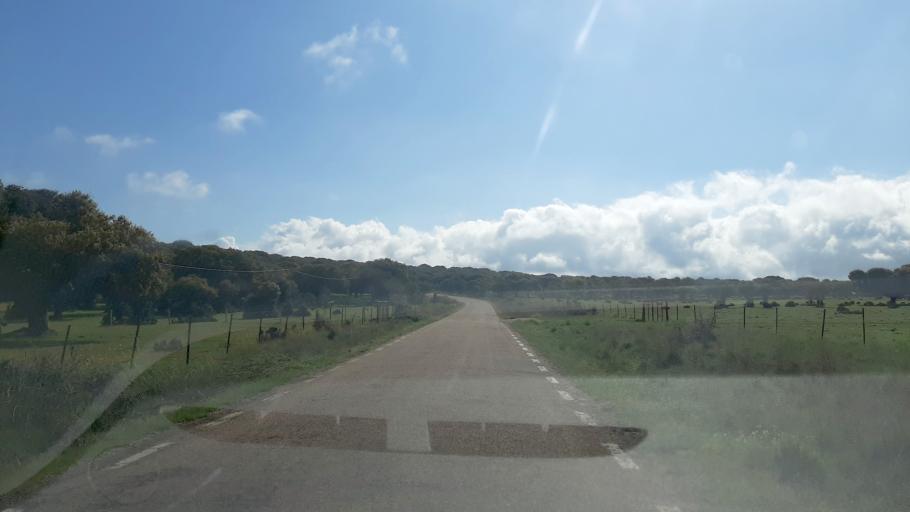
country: ES
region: Castille and Leon
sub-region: Provincia de Salamanca
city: Narros de Matalayegua
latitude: 40.7042
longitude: -5.8971
